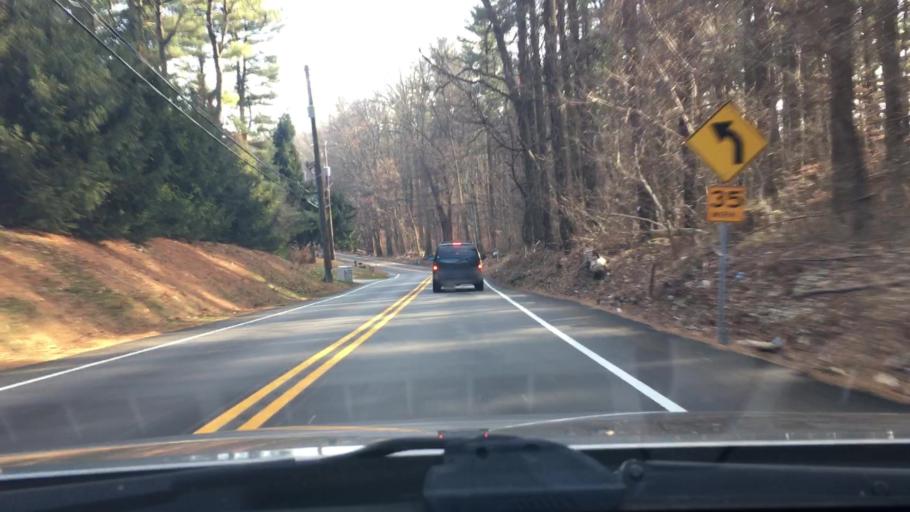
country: US
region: Pennsylvania
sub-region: Delaware County
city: Lima
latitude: 39.9705
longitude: -75.4444
